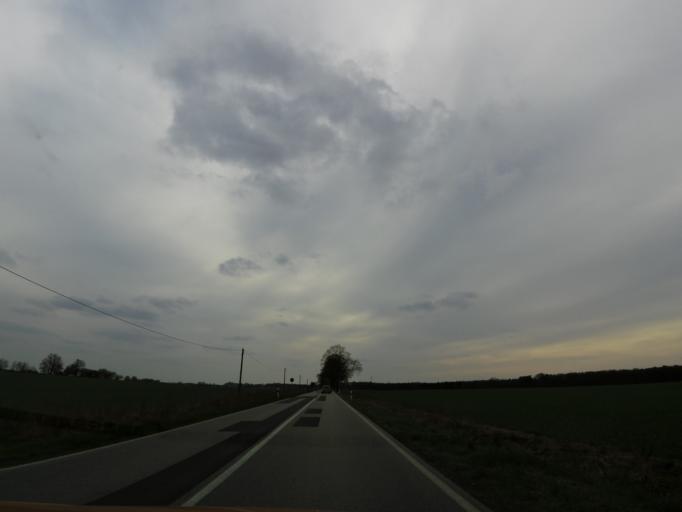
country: DE
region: Brandenburg
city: Beeskow
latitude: 52.2069
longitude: 14.3114
